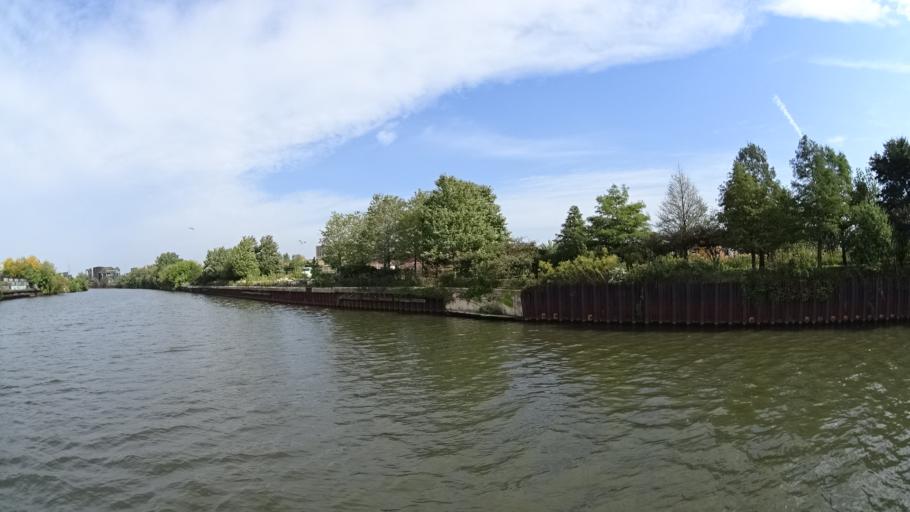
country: US
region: Illinois
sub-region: Cook County
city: Chicago
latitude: 41.9110
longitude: -87.6580
